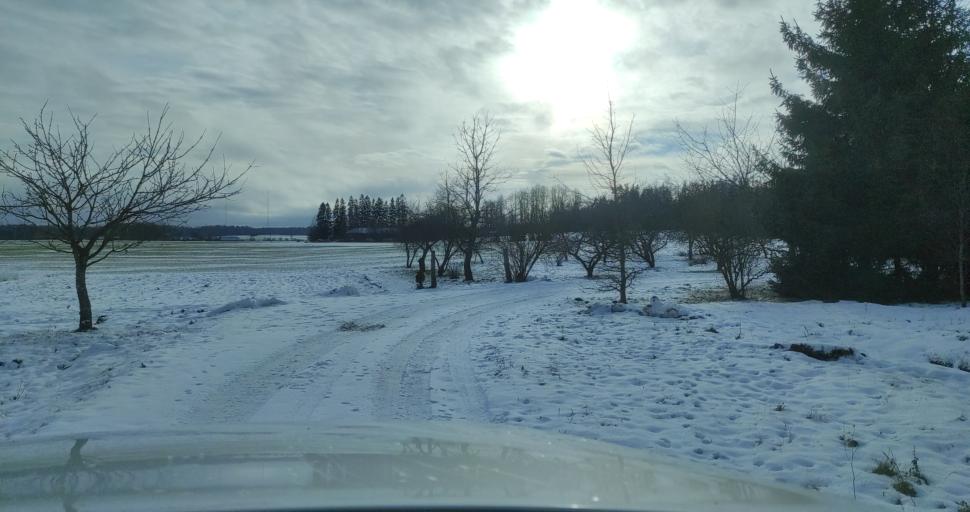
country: LV
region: Kuldigas Rajons
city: Kuldiga
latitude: 56.9655
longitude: 21.8914
